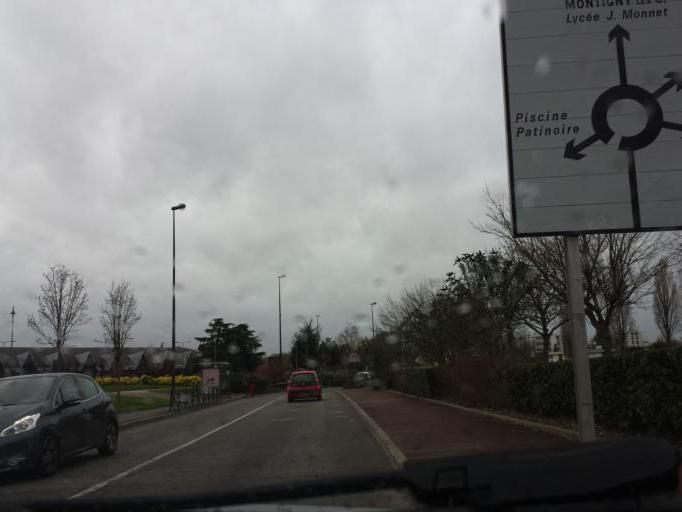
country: FR
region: Ile-de-France
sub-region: Departement du Val-d'Oise
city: Le Plessis-Bouchard
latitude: 48.9917
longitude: 2.2244
